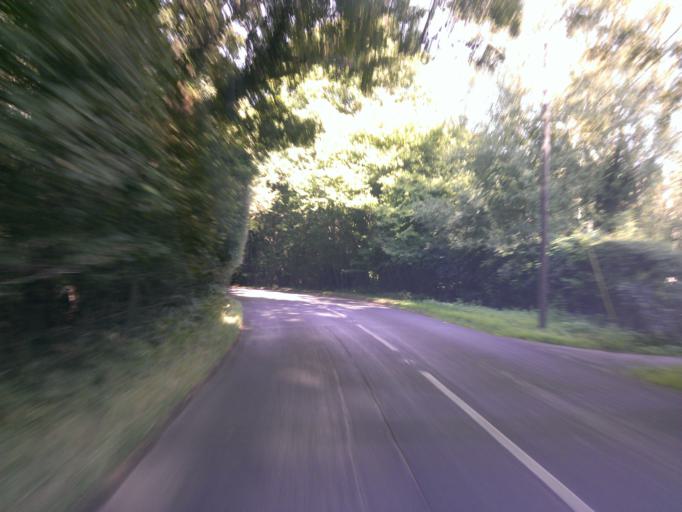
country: GB
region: England
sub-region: Kent
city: Sevenoaks
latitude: 51.1961
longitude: 0.1926
